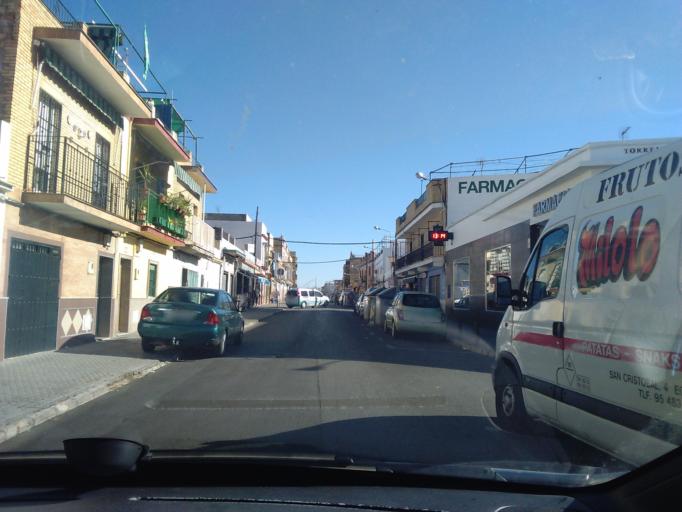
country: ES
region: Andalusia
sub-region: Provincia de Sevilla
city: Sevilla
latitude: 37.3853
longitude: -5.9058
